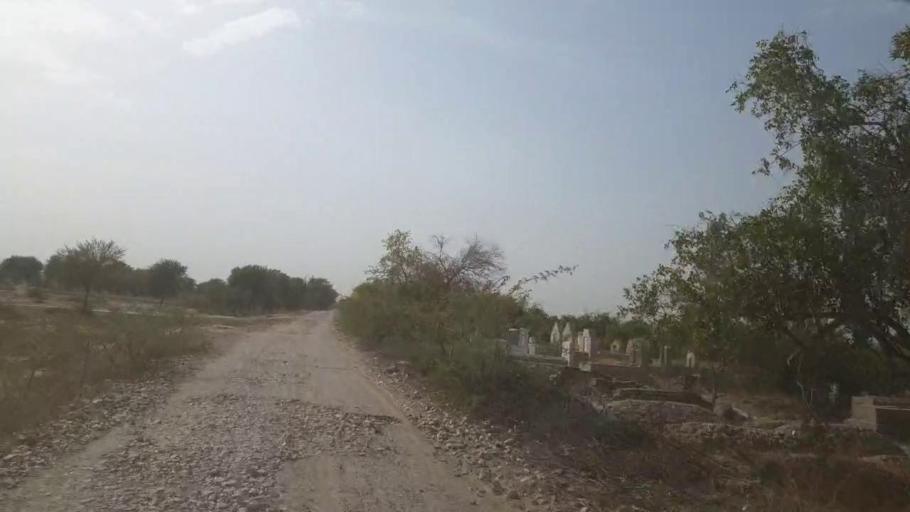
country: PK
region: Sindh
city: Nabisar
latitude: 25.0382
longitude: 69.5049
